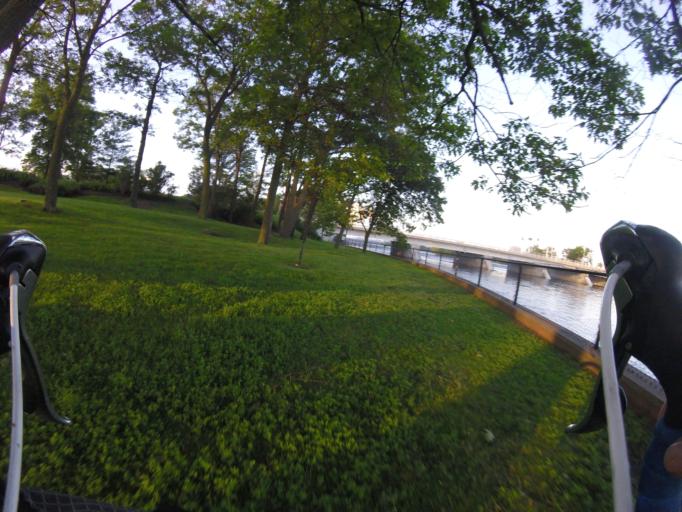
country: CA
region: Ontario
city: Ottawa
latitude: 45.4076
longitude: -75.7576
